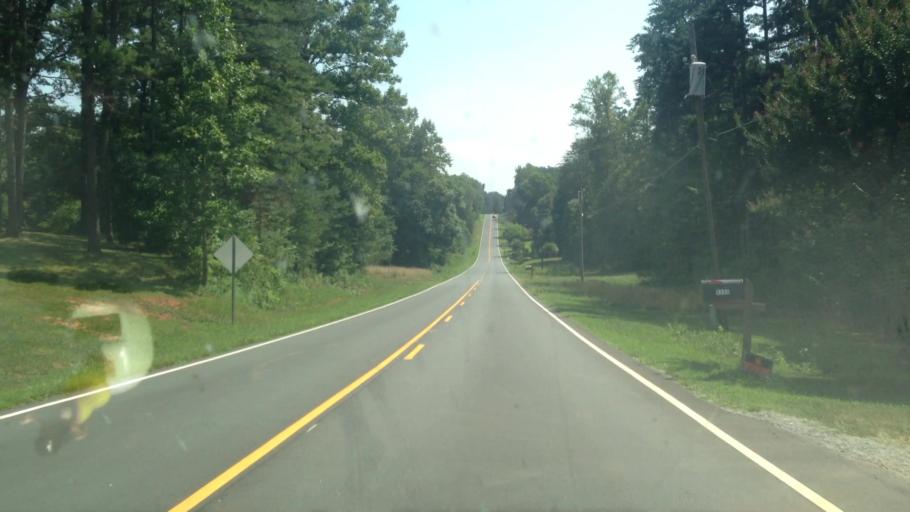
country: US
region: North Carolina
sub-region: Rockingham County
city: Mayodan
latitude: 36.4191
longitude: -80.0847
